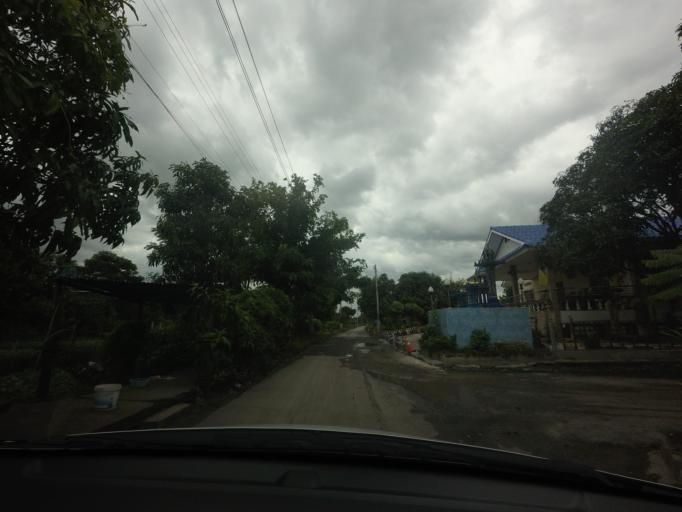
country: TH
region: Bangkok
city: Min Buri
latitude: 13.7773
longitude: 100.7685
